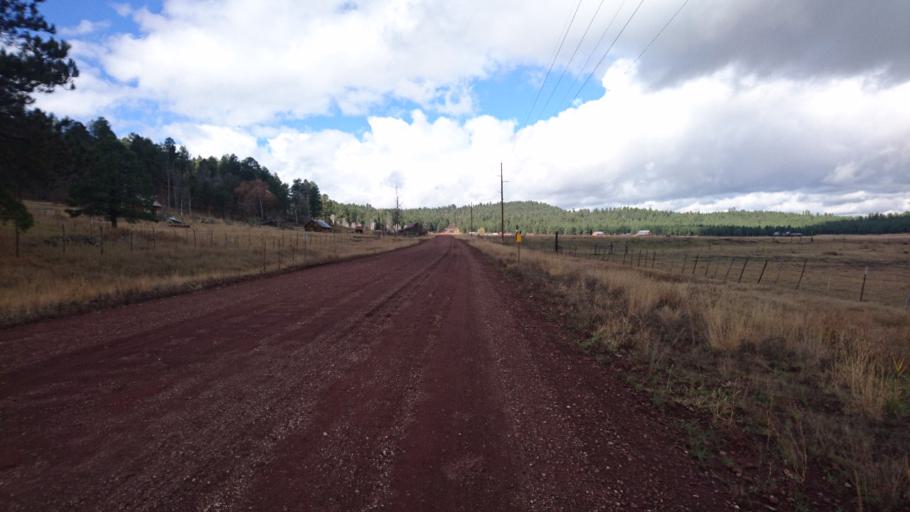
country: US
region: Arizona
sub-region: Coconino County
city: Parks
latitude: 35.2699
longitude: -111.8868
